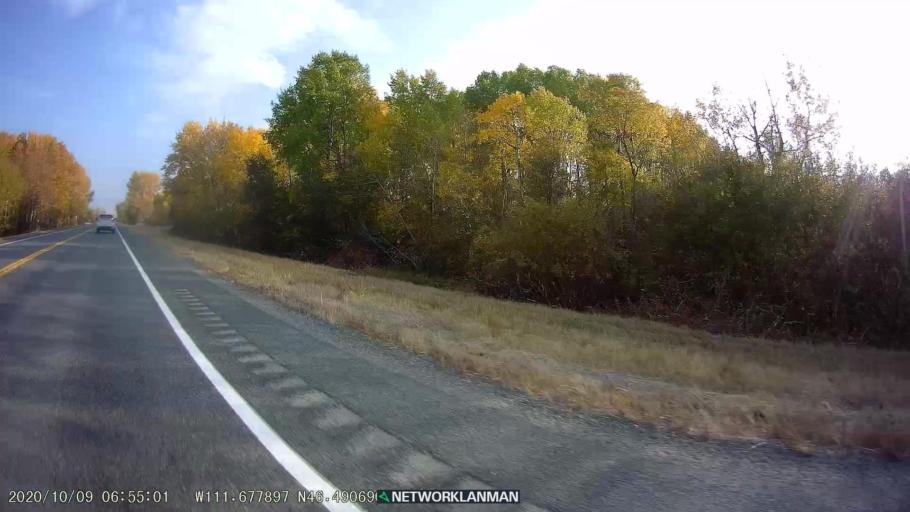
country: US
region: Montana
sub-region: Broadwater County
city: Townsend
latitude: 46.4899
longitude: -111.6783
